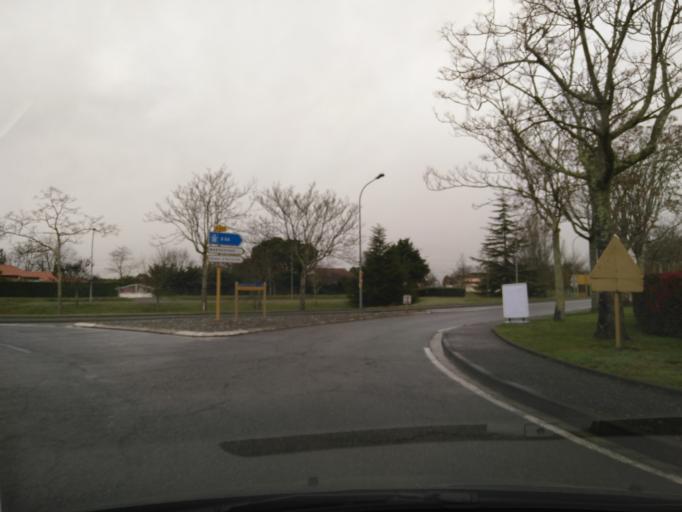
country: FR
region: Midi-Pyrenees
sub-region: Departement de la Haute-Garonne
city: Carbonne
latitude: 43.3022
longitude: 1.2204
